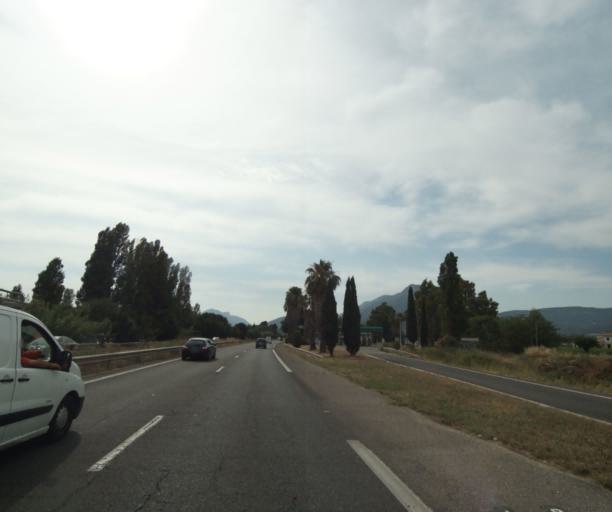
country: FR
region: Provence-Alpes-Cote d'Azur
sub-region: Departement du Var
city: La Crau
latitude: 43.1340
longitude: 6.0499
